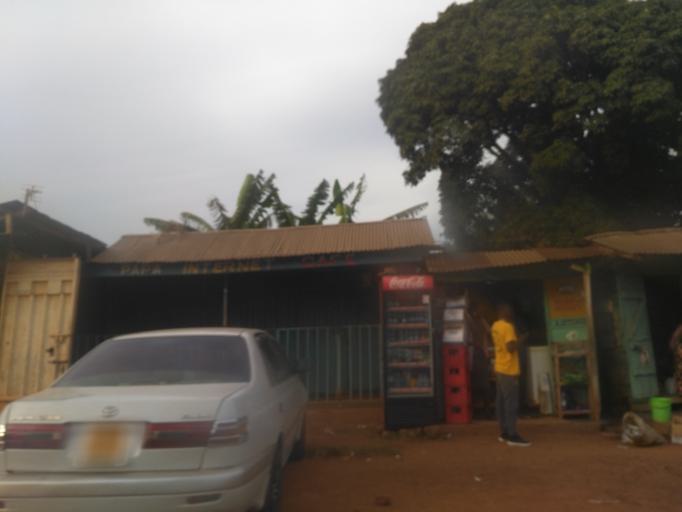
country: UG
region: Central Region
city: Kampala Central Division
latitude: 0.3435
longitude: 32.5780
